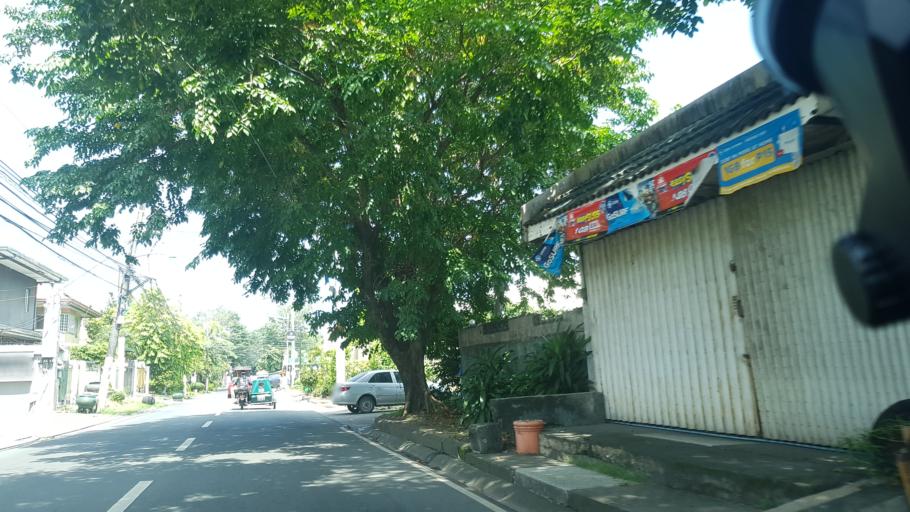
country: PH
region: Calabarzon
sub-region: Province of Rizal
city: Las Pinas
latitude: 14.4367
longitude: 120.9915
